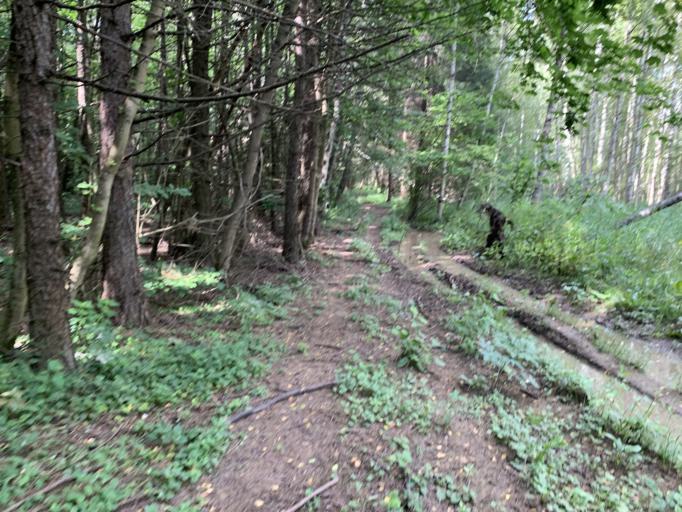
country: RU
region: Moskovskaya
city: Podosinki
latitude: 56.1792
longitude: 37.5678
